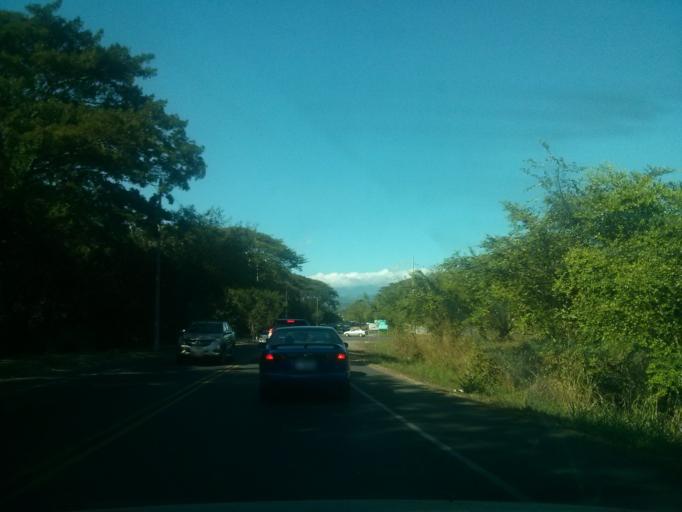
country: CR
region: Puntarenas
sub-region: Canton Central de Puntarenas
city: Chacarita
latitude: 9.9793
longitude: -84.7398
